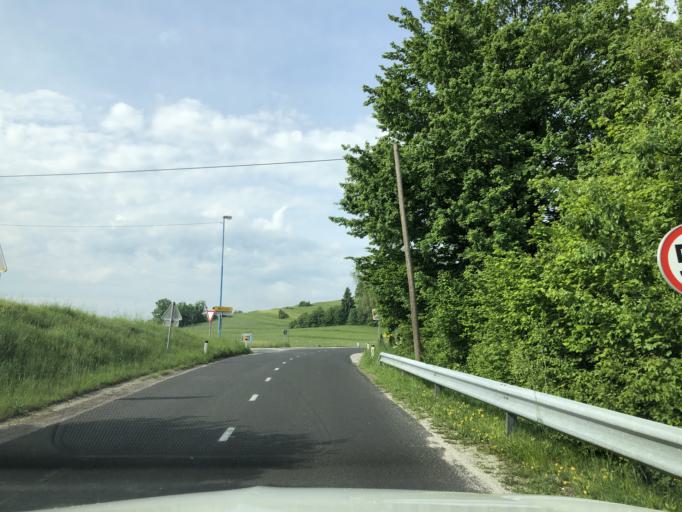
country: SI
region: Velike Lasce
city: Velike Lasce
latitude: 45.8153
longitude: 14.6259
